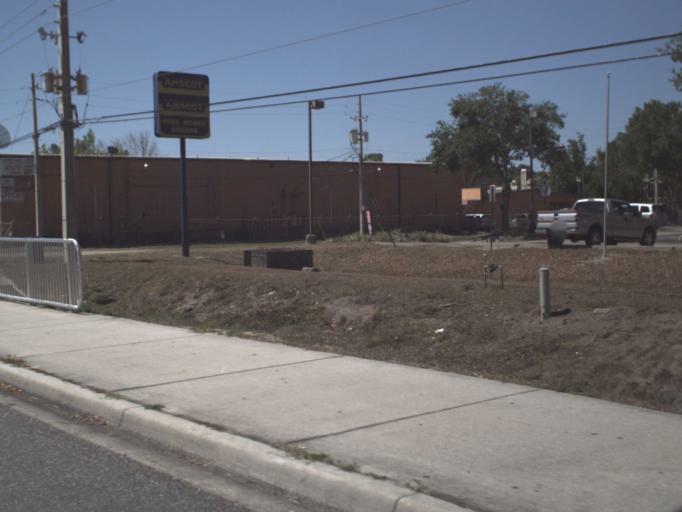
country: US
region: Florida
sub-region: Orange County
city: Conway
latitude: 28.5011
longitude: -81.3104
